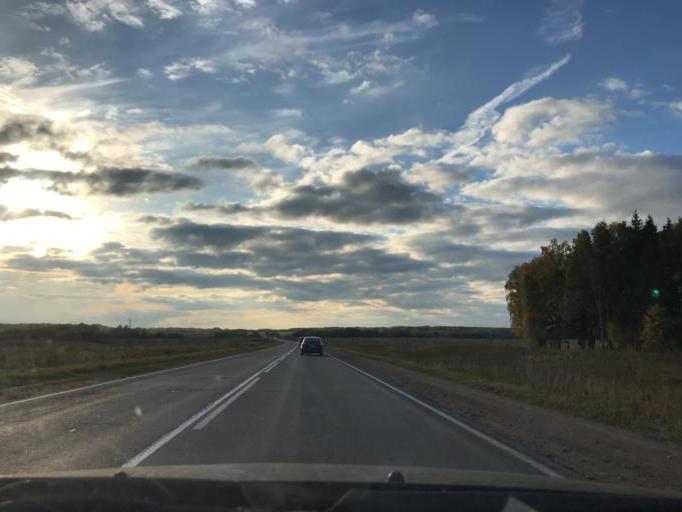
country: RU
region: Kaluga
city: Kurovskoye
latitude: 54.5289
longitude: 35.9326
